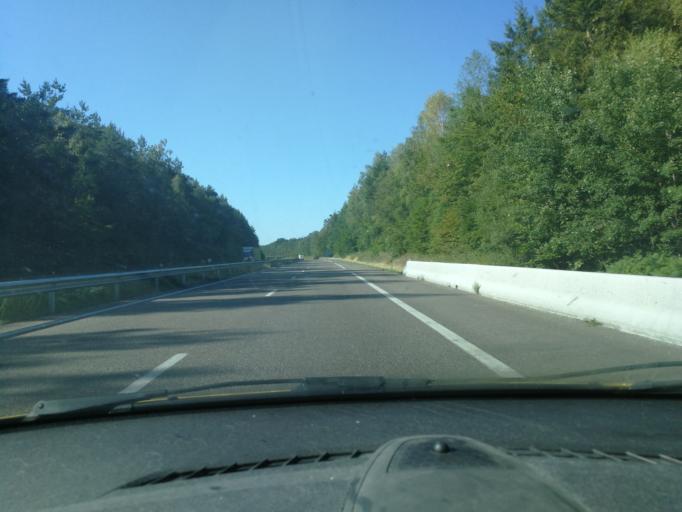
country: FR
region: Alsace
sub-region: Departement du Bas-Rhin
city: Herbitzheim
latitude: 48.9965
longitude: 7.0653
